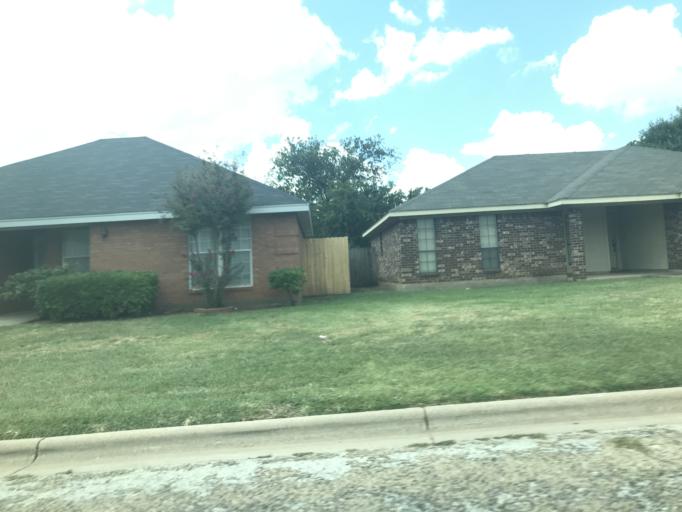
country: US
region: Texas
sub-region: Taylor County
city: Abilene
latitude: 32.4431
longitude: -99.6999
